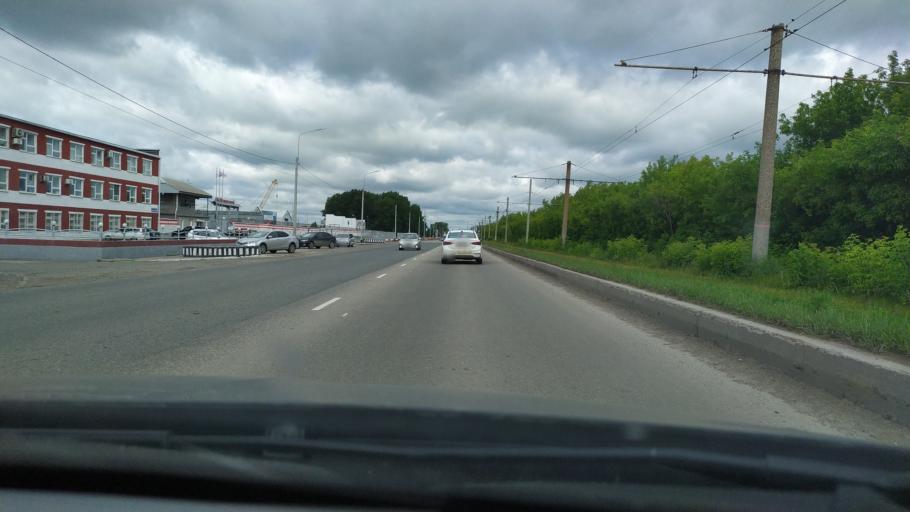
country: RU
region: Perm
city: Kondratovo
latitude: 57.9269
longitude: 56.1345
